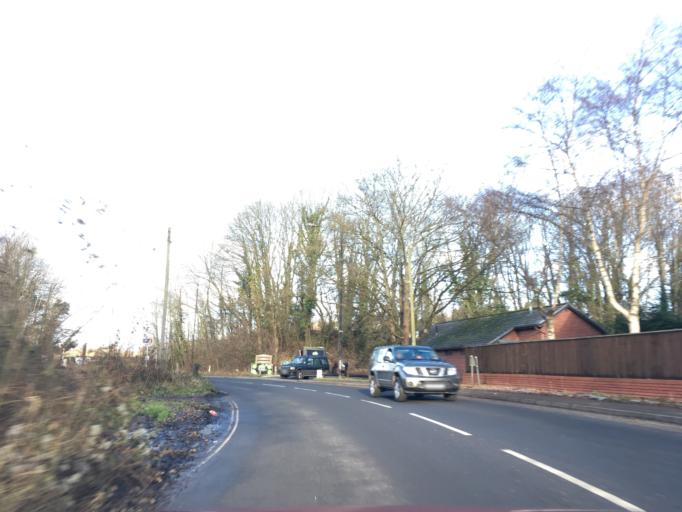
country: GB
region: Wales
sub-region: Monmouthshire
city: Usk
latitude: 51.7057
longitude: -2.9091
